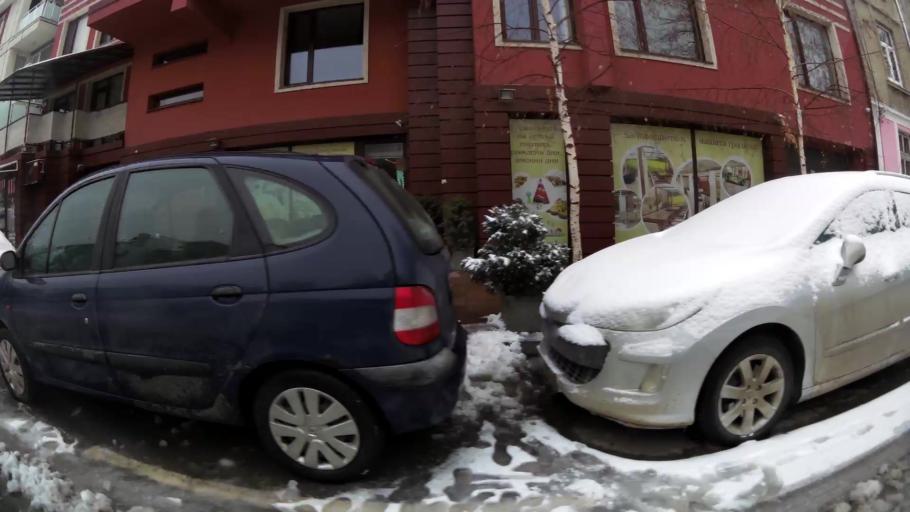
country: BG
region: Sofia-Capital
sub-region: Stolichna Obshtina
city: Sofia
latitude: 42.7058
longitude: 23.3309
